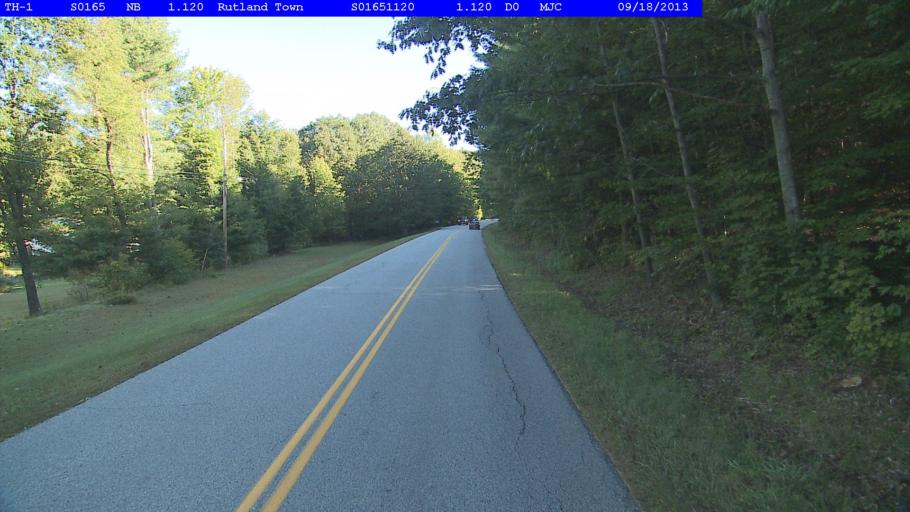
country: US
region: Vermont
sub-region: Rutland County
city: Rutland
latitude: 43.6562
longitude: -72.9533
